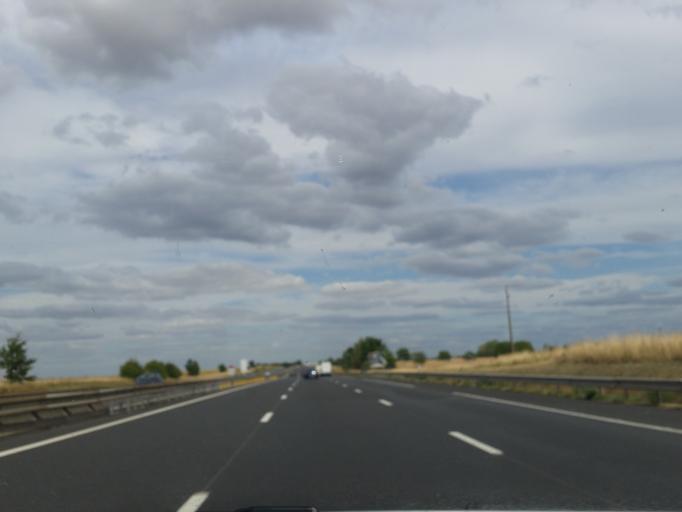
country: FR
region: Centre
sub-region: Departement d'Indre-et-Loire
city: Reugny
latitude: 47.4982
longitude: 0.8486
